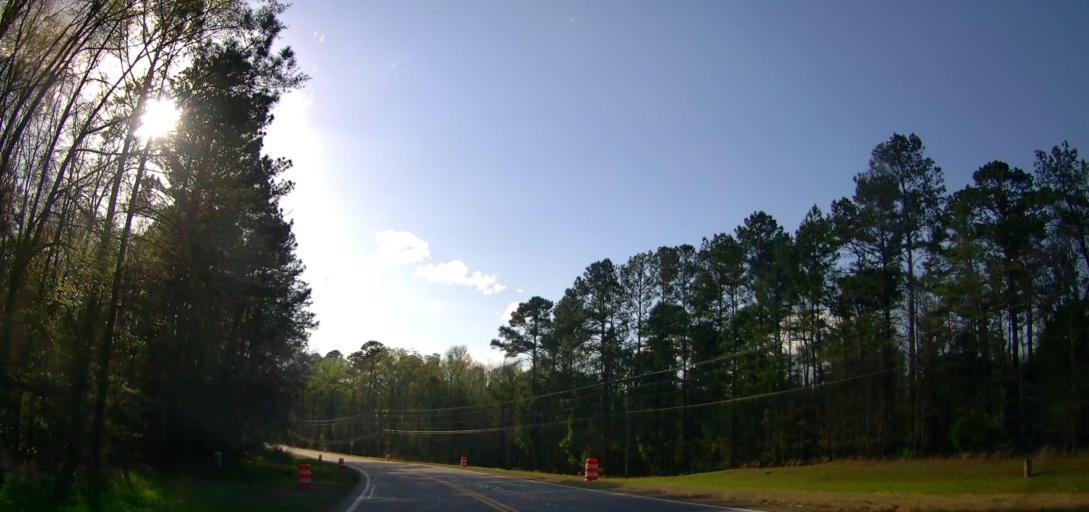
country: US
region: Georgia
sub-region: Baldwin County
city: Milledgeville
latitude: 33.1596
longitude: -83.3546
